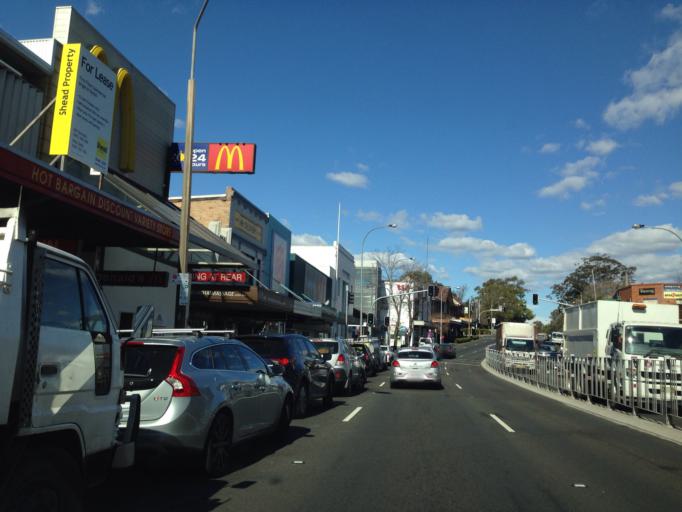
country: AU
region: New South Wales
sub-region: Ku-ring-gai
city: Killara
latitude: -33.7552
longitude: 151.1526
